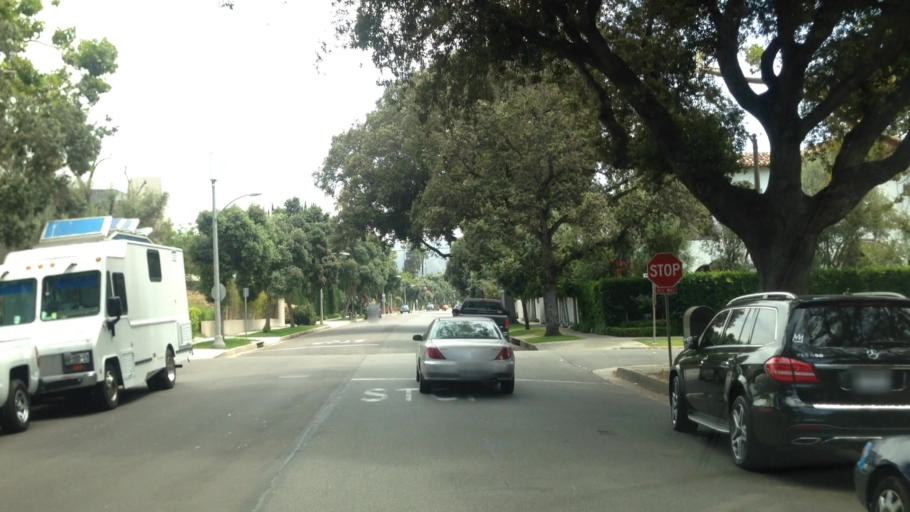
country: US
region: California
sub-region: Los Angeles County
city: Beverly Hills
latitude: 34.0700
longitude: -118.4146
